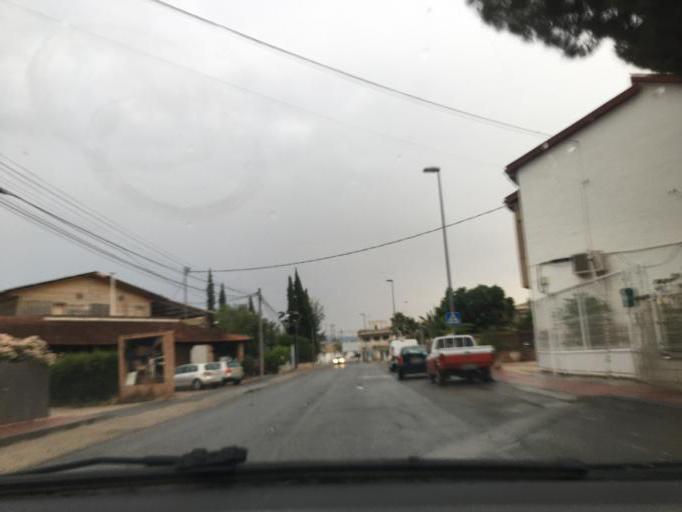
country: ES
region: Murcia
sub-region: Murcia
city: Santomera
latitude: 38.0278
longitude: -1.0463
